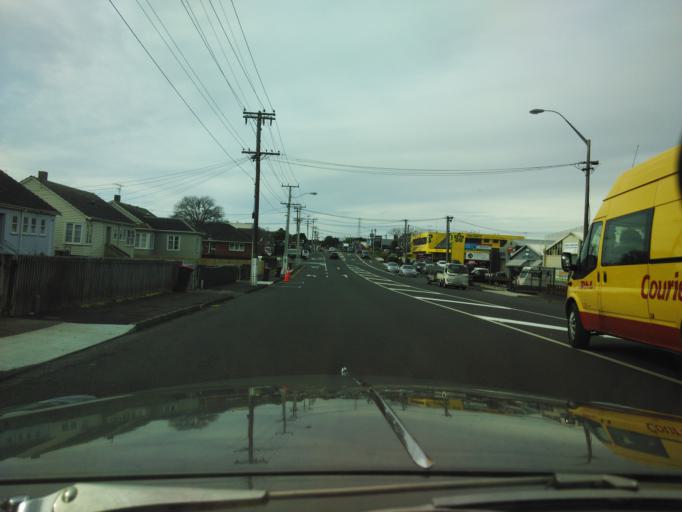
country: NZ
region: Auckland
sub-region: Auckland
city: Mangere
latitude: -36.9145
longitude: 174.8044
